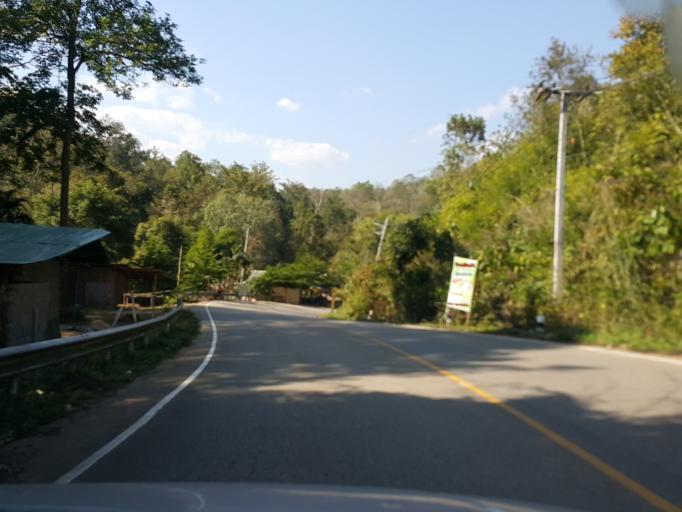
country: TH
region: Chiang Mai
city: Mae Wang
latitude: 18.6353
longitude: 98.7046
